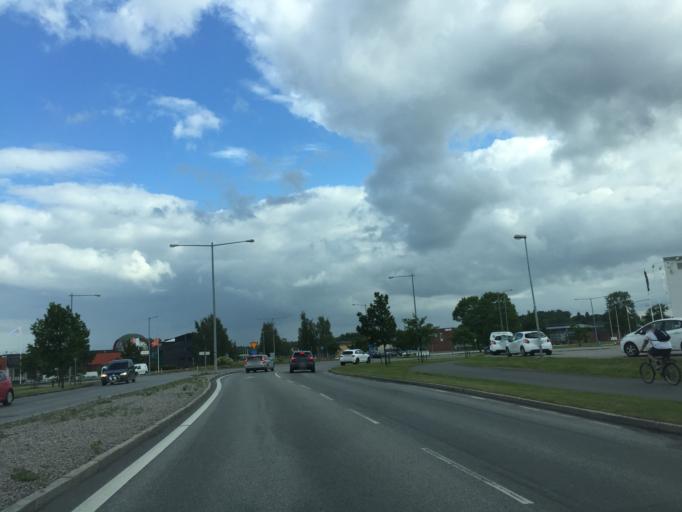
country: SE
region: OErebro
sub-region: Orebro Kommun
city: Orebro
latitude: 59.2607
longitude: 15.1748
